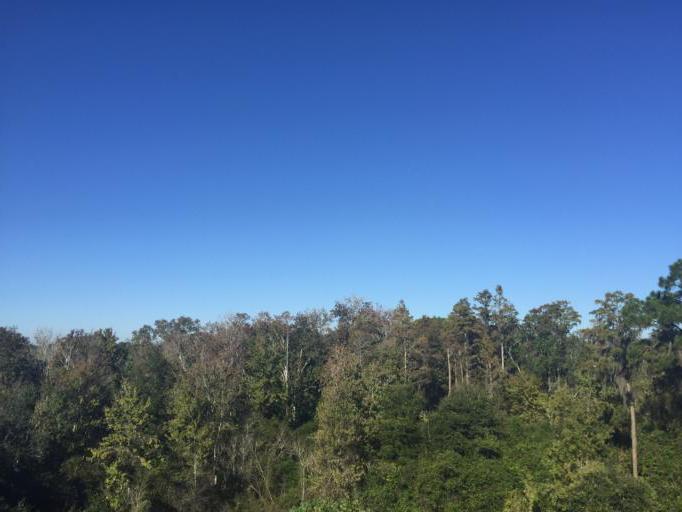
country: US
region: Florida
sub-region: Orange County
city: Bay Hill
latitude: 28.4139
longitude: -81.5883
